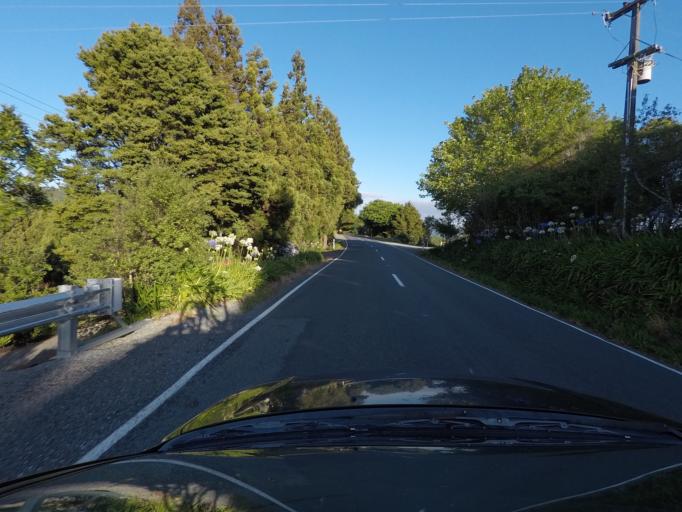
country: NZ
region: Northland
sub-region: Whangarei
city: Whangarei
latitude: -35.6557
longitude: 174.3104
